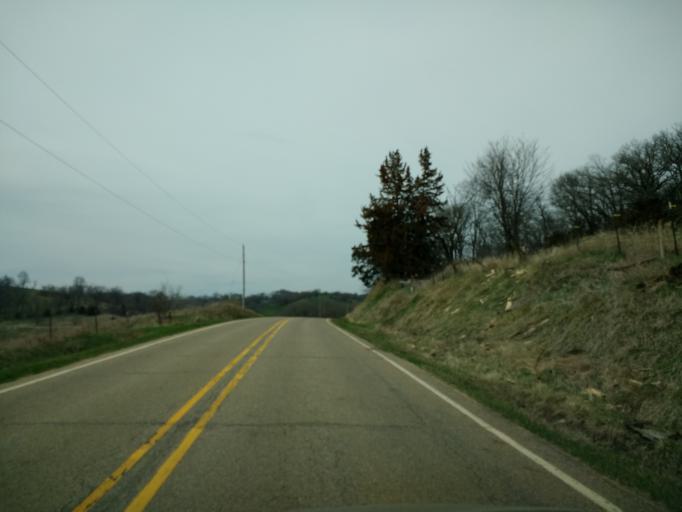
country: US
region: Iowa
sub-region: Monona County
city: Mapleton
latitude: 42.2351
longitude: -95.9468
